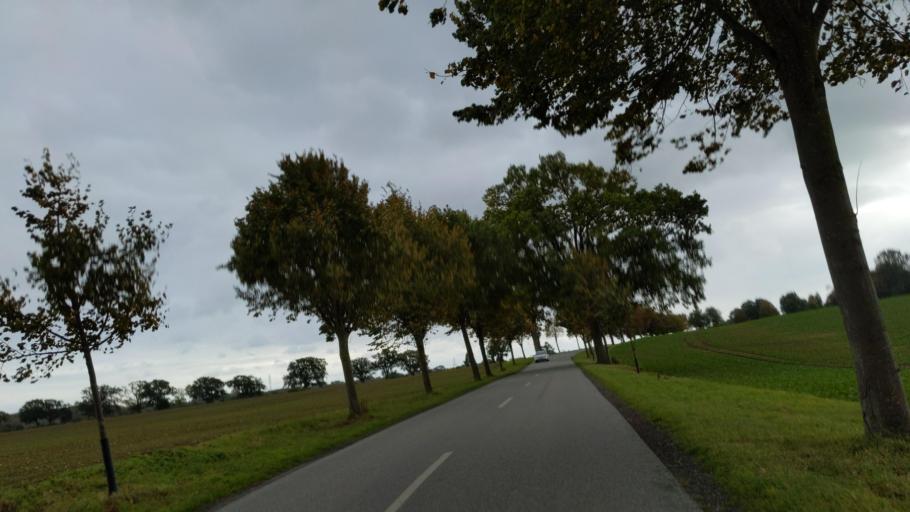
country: DE
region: Schleswig-Holstein
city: Neustadt in Holstein
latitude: 54.1232
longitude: 10.7791
